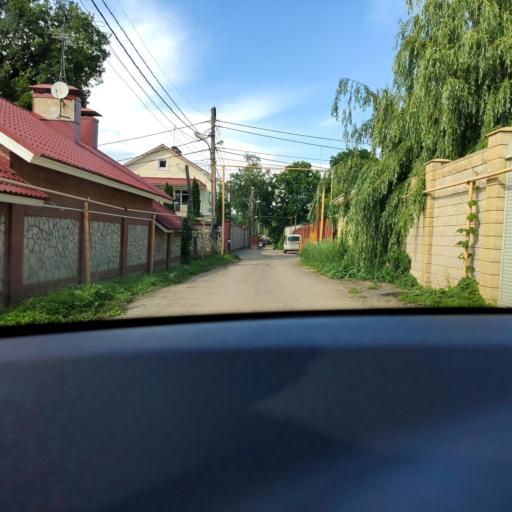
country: RU
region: Samara
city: Samara
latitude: 53.2728
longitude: 50.2098
